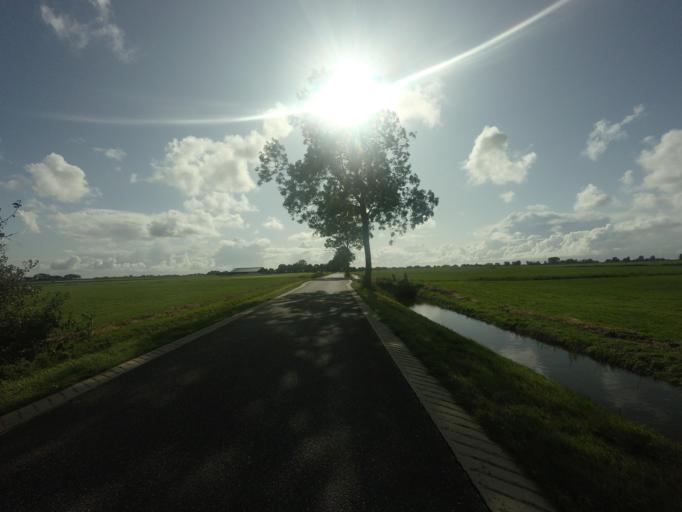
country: NL
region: Friesland
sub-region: Sudwest Fryslan
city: Bolsward
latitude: 53.0330
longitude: 5.5026
